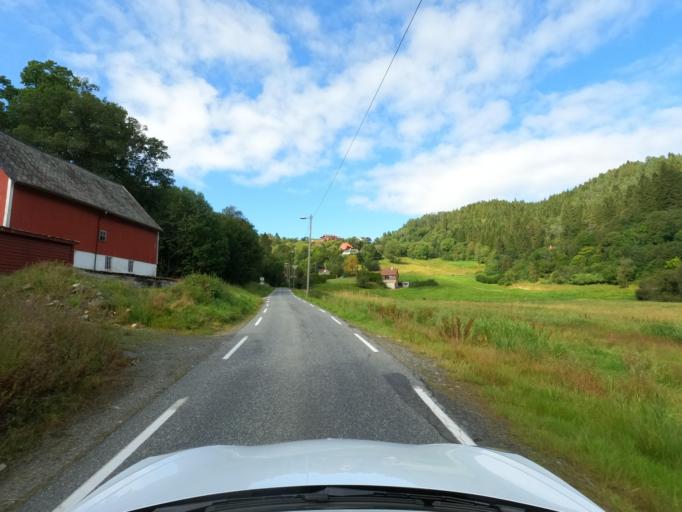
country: NO
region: Hordaland
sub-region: Bergen
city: Sandsli
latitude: 60.2767
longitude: 5.3544
